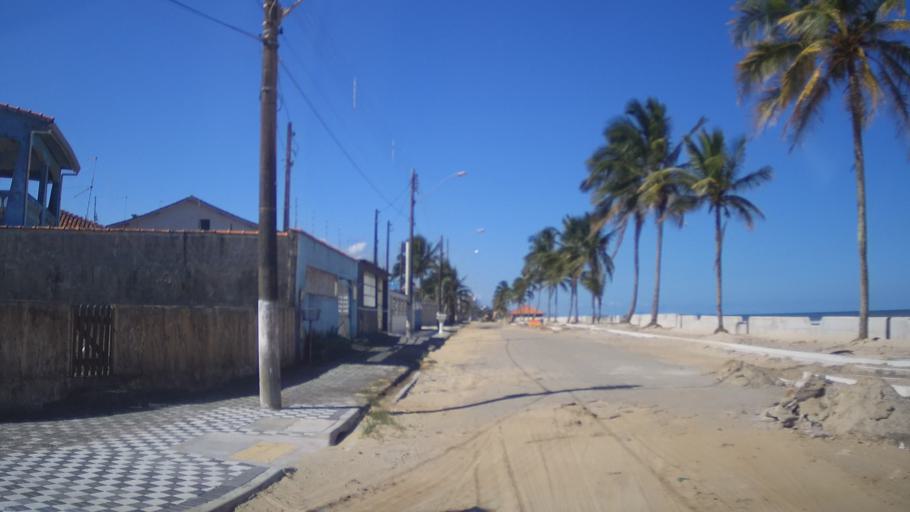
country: BR
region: Sao Paulo
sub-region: Mongagua
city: Mongagua
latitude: -24.1279
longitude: -46.6825
